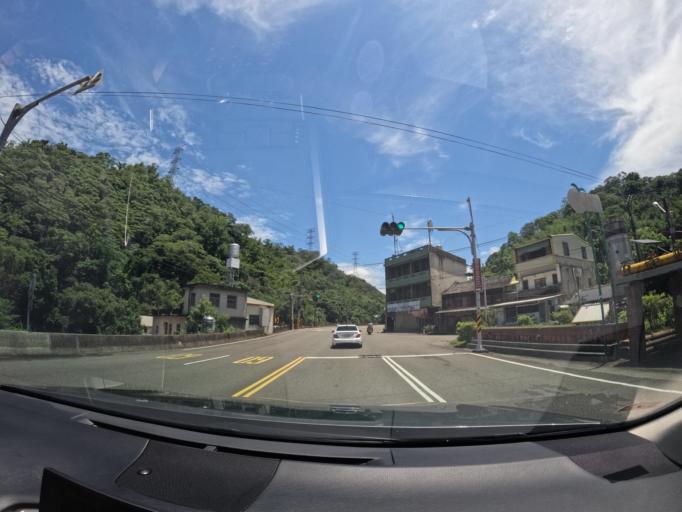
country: TW
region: Taiwan
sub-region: Miaoli
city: Miaoli
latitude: 24.5798
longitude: 120.9403
